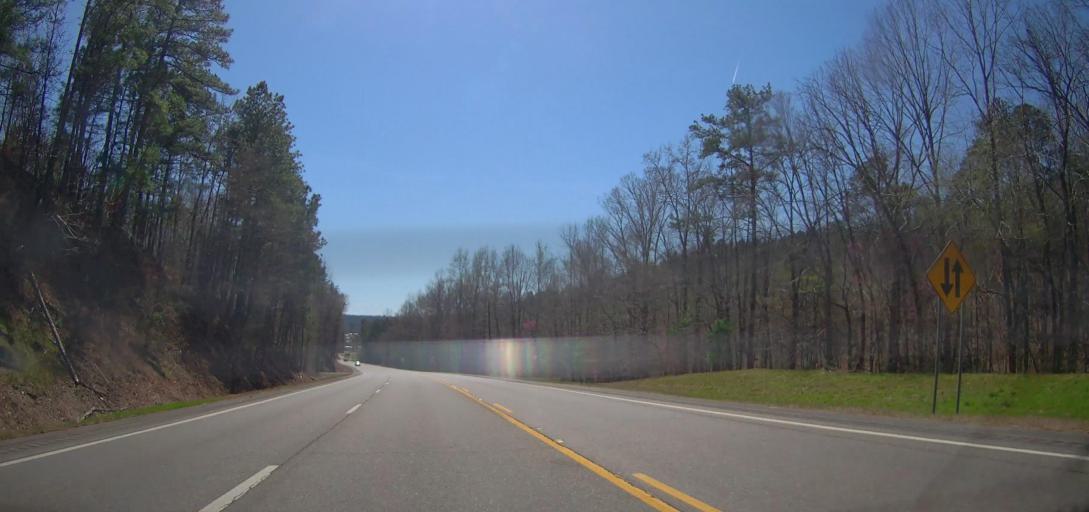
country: US
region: Alabama
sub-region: Calhoun County
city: Ohatchee
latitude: 33.8409
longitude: -86.0510
